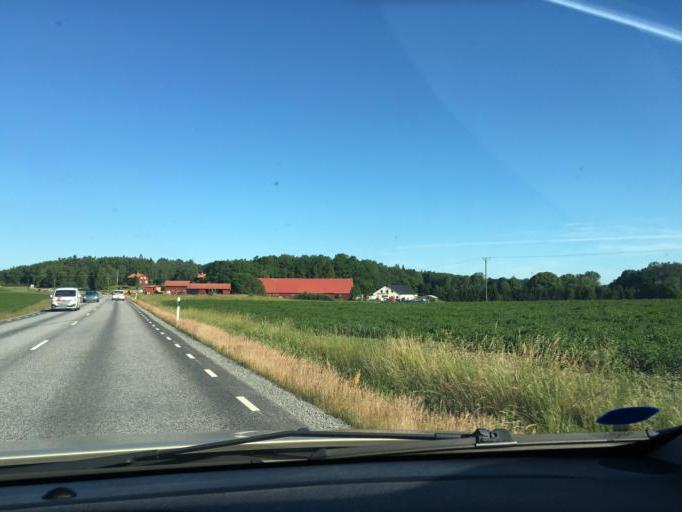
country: SE
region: Stockholm
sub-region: Salems Kommun
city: Ronninge
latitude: 59.2191
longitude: 17.7570
